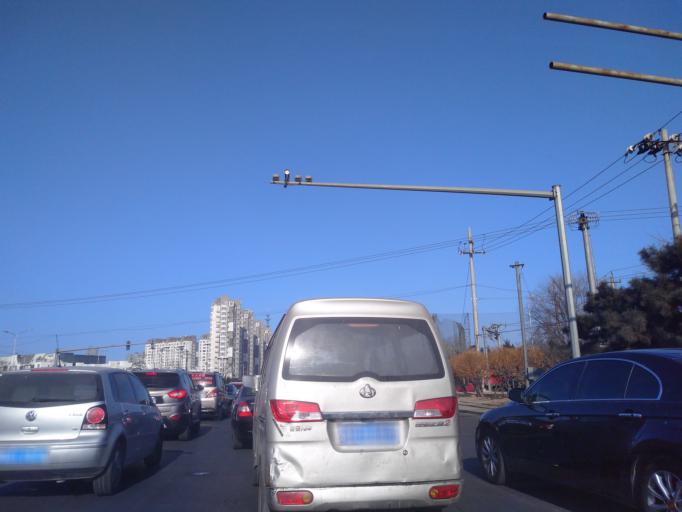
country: CN
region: Beijing
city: Jiugong
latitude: 39.8235
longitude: 116.4757
